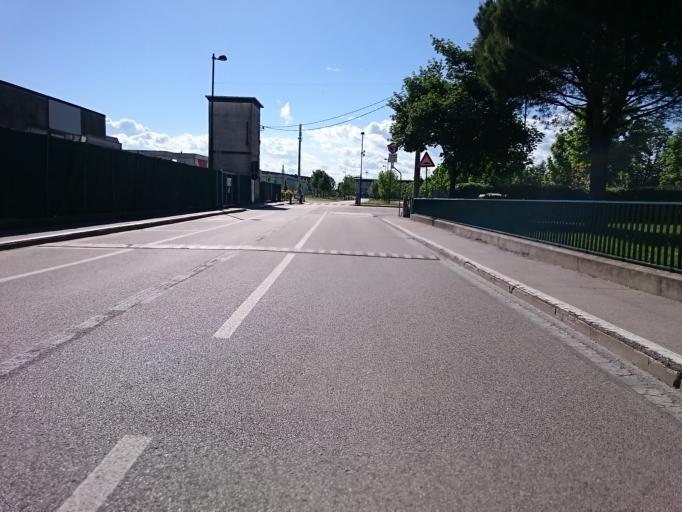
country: IT
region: Veneto
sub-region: Provincia di Padova
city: Legnaro
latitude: 45.3447
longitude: 11.9621
